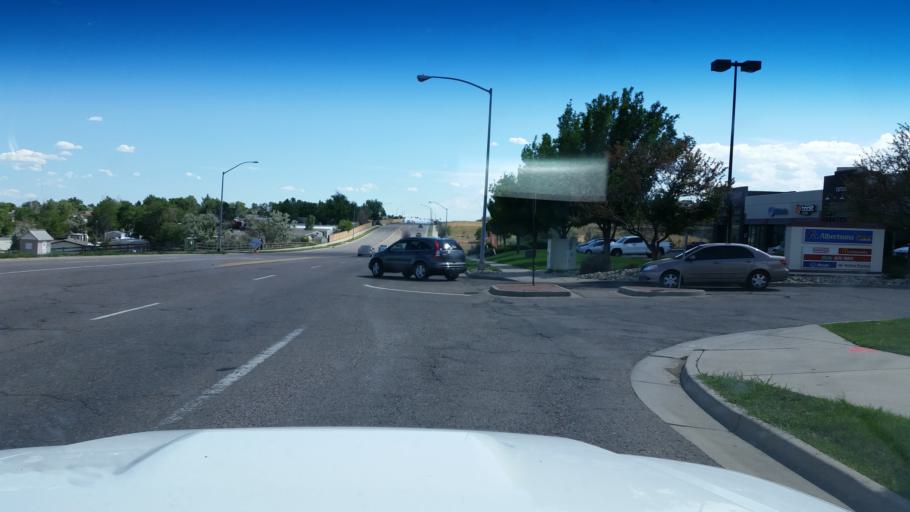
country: US
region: Colorado
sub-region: Adams County
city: Thornton
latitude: 39.8834
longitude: -104.9404
